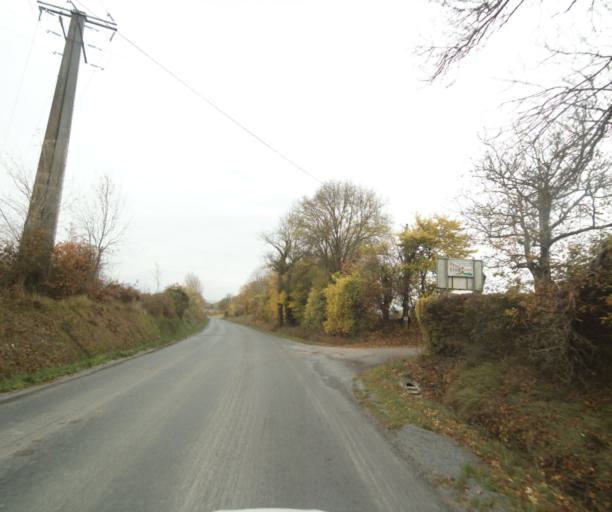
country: FR
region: Poitou-Charentes
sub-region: Departement de la Charente-Maritime
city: Chermignac
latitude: 45.7066
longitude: -0.6567
